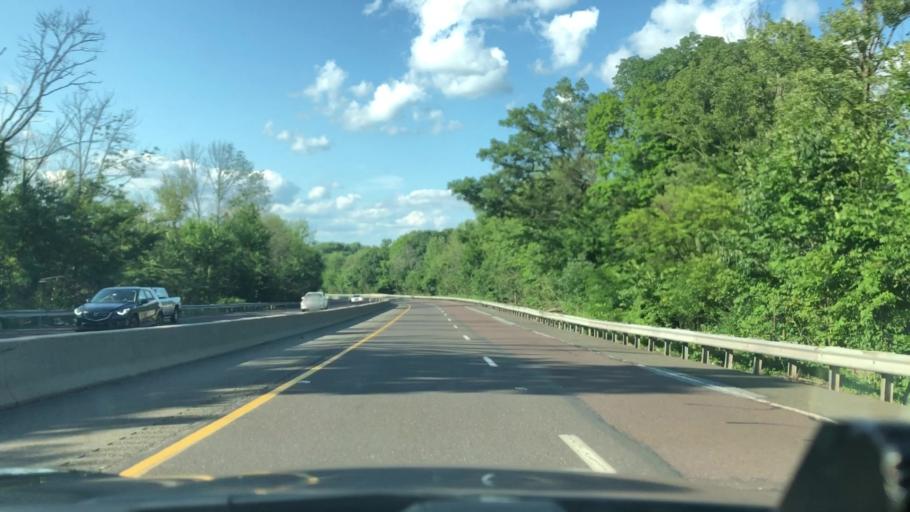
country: US
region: Pennsylvania
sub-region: Bucks County
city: Quakertown
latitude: 40.3989
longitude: -75.3368
